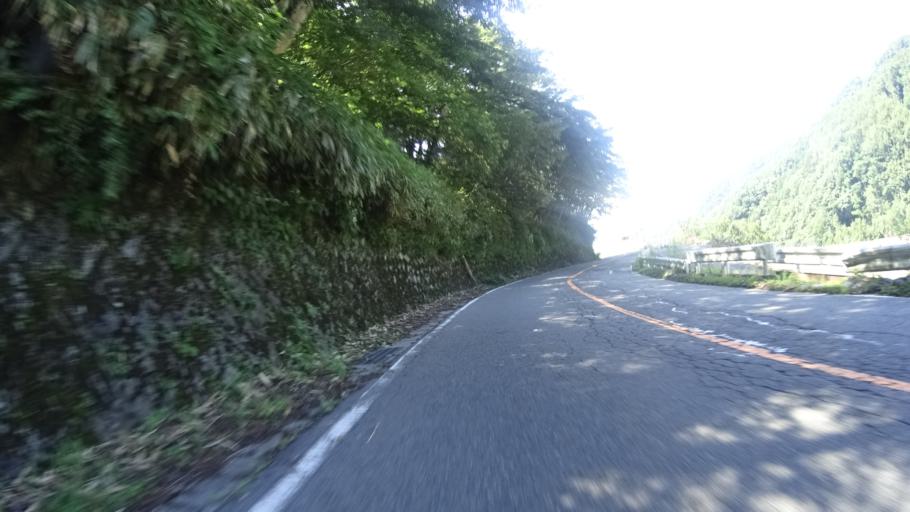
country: JP
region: Yamanashi
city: Enzan
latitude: 35.7723
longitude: 138.8041
